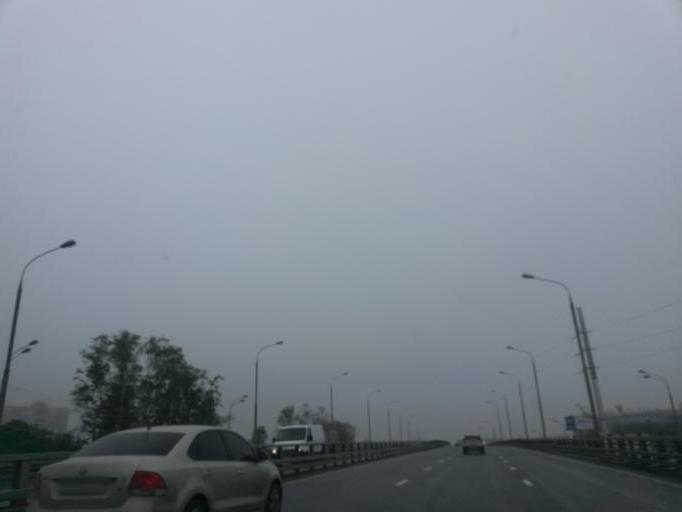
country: RU
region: Moscow
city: Tyoply Stan
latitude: 55.6166
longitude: 37.5018
